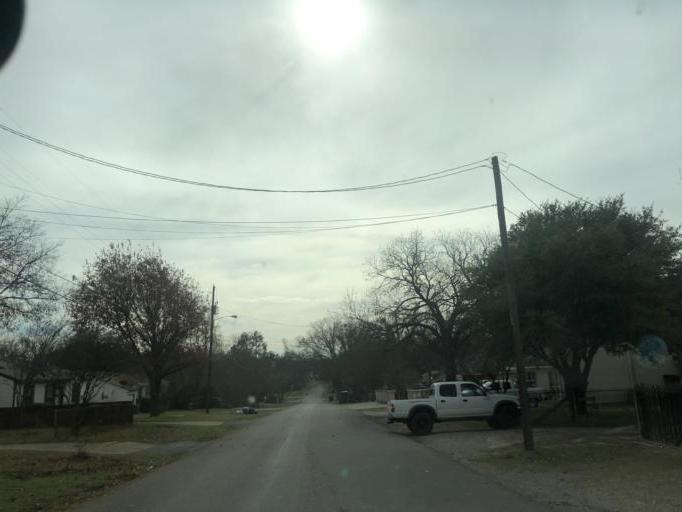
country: US
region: Texas
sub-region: Dallas County
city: Duncanville
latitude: 32.6683
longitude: -96.8337
